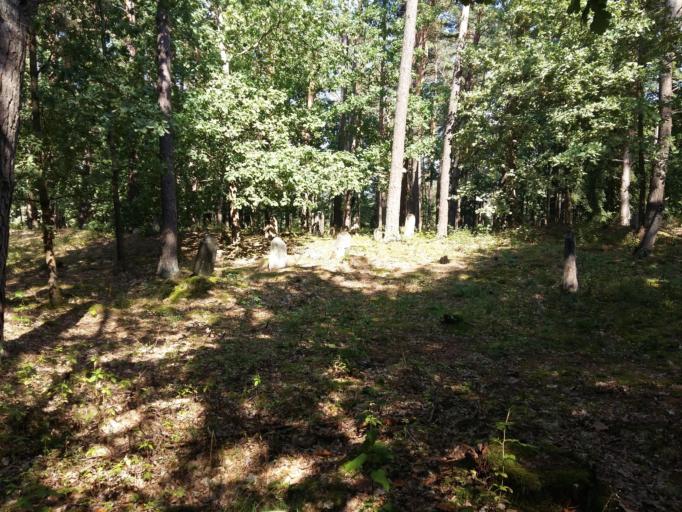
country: LT
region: Alytaus apskritis
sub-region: Alytaus rajonas
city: Daugai
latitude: 54.1632
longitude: 24.1976
